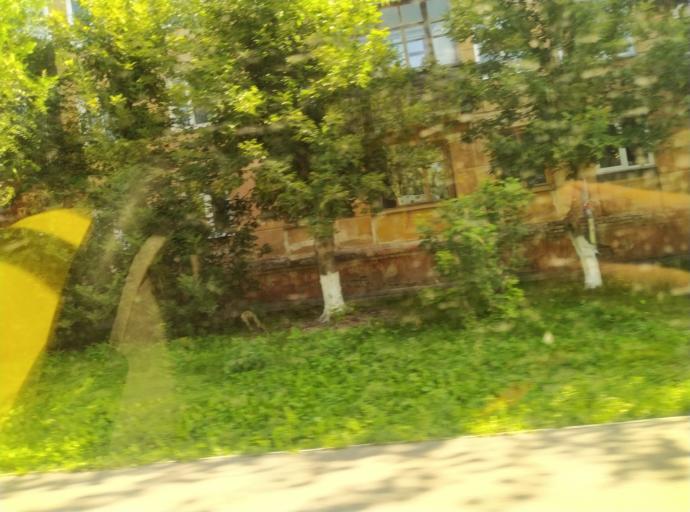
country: RU
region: Krasnoyarskiy
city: Krasnoyarsk
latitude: 55.9771
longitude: 92.8429
